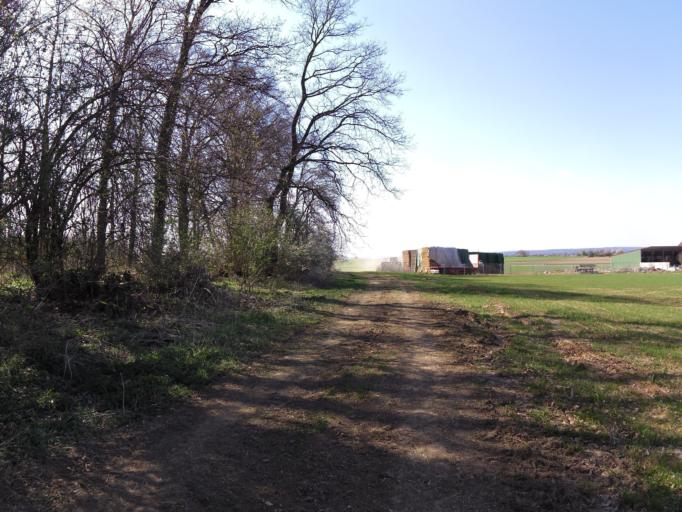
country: DE
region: Bavaria
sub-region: Regierungsbezirk Unterfranken
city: Kurnach
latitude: 49.8333
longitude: 10.0552
